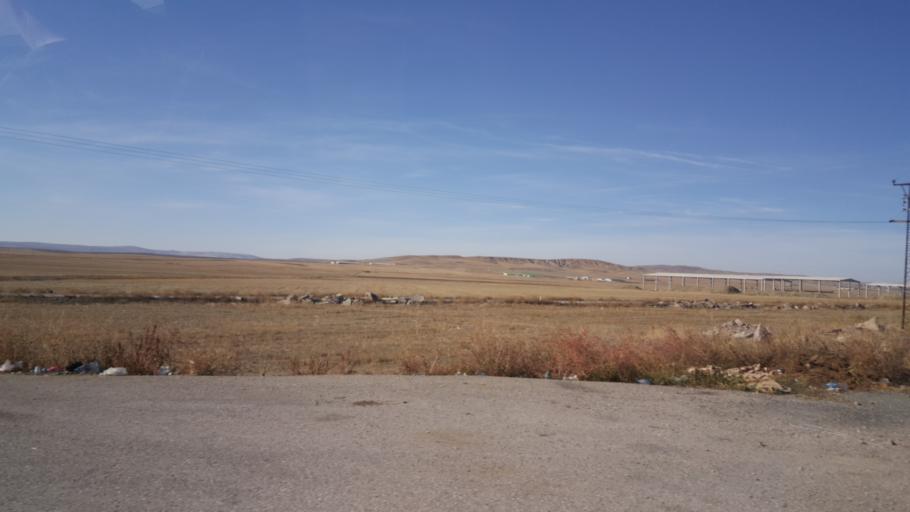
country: TR
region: Ankara
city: Yenice
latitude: 39.4090
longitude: 32.8698
